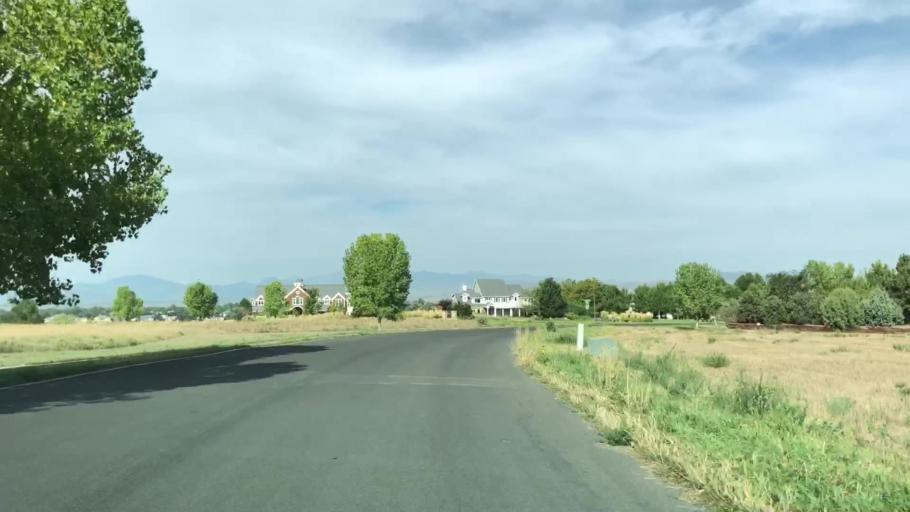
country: US
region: Colorado
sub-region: Larimer County
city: Loveland
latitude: 40.4371
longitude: -105.0530
